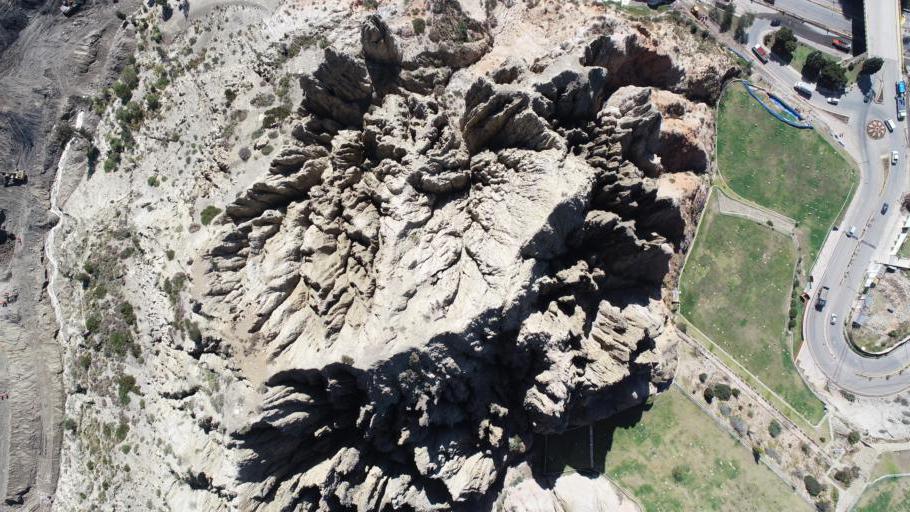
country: BO
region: La Paz
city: La Paz
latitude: -16.5202
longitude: -68.1198
